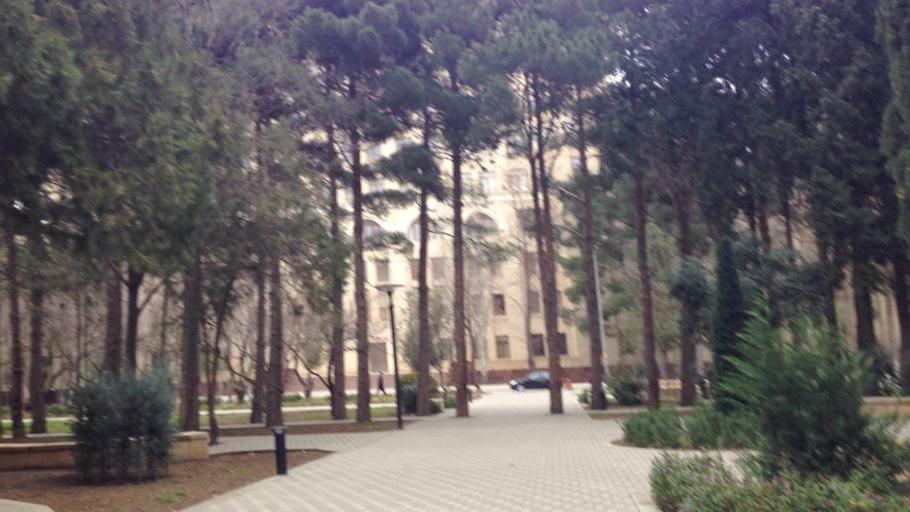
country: AZ
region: Baki
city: Badamdar
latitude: 40.3730
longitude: 49.8126
